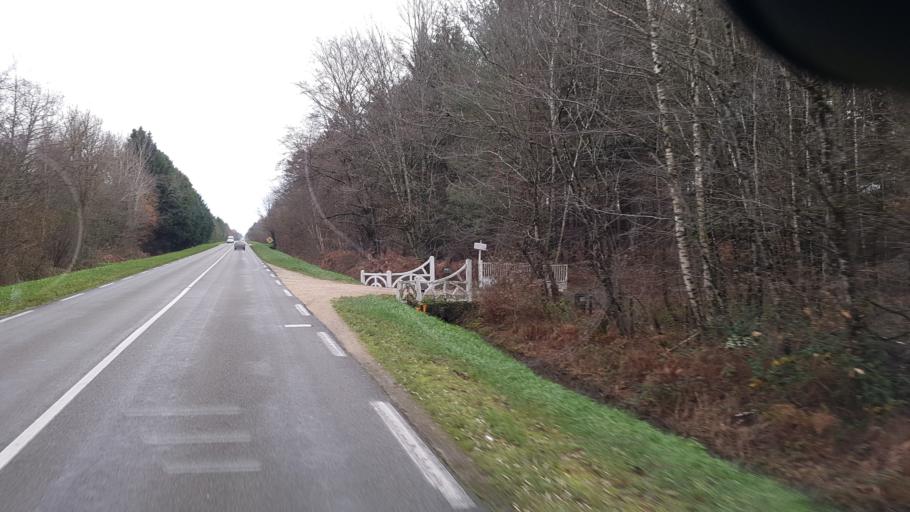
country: FR
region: Centre
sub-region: Departement du Loiret
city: La Ferte-Saint-Aubin
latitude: 47.6714
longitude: 1.9722
